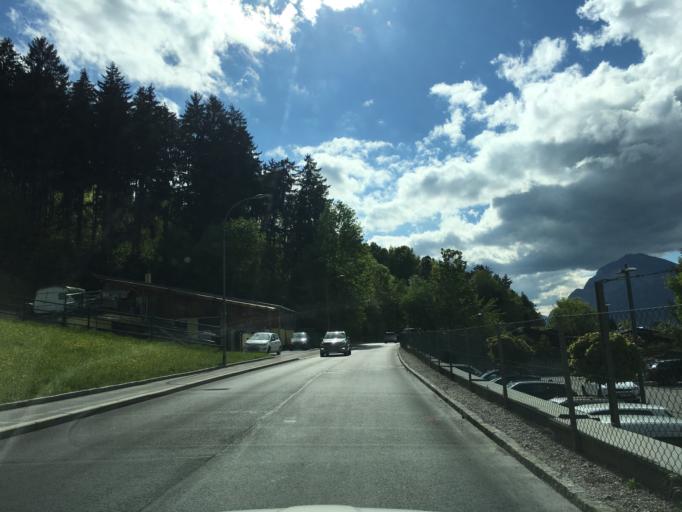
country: AT
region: Tyrol
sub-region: Politischer Bezirk Innsbruck Land
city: Ampass
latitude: 47.2599
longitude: 11.4467
